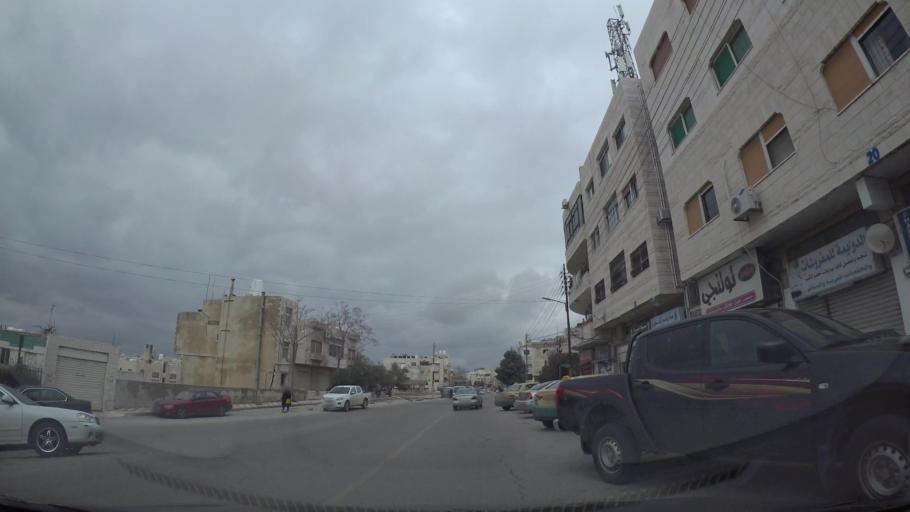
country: JO
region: Amman
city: Wadi as Sir
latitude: 31.9563
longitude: 35.8349
